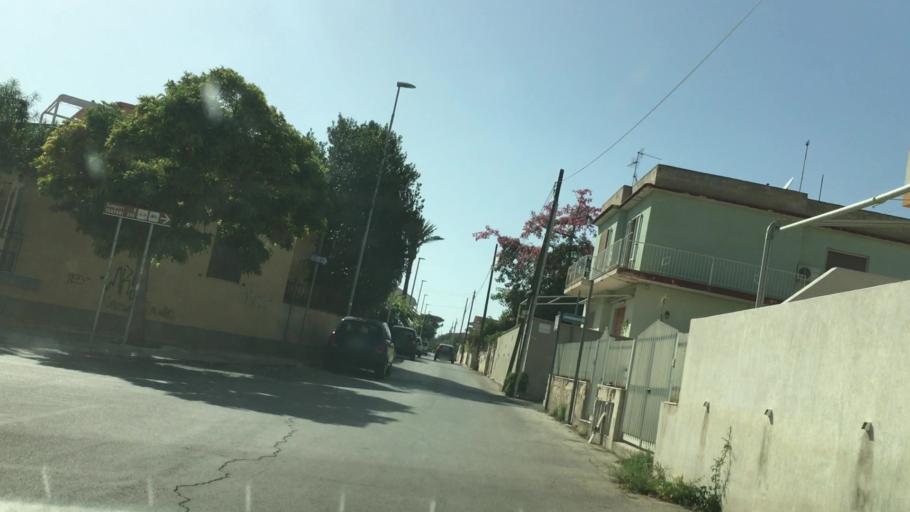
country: IT
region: Sicily
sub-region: Ragusa
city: Pozzallo
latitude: 36.7146
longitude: 14.7788
